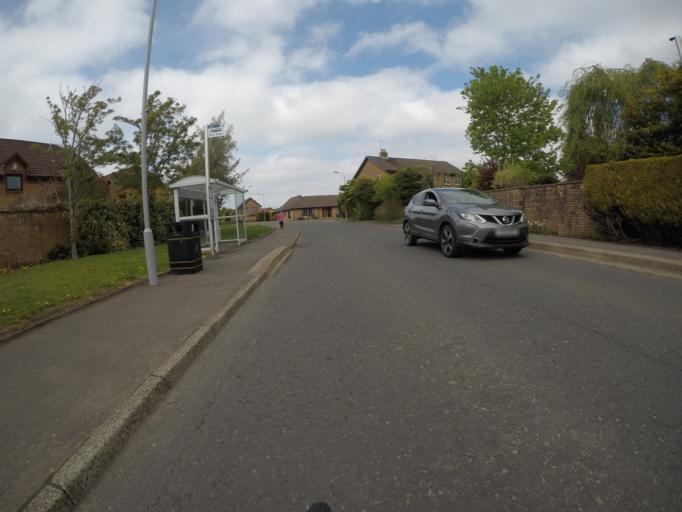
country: GB
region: Scotland
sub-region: East Renfrewshire
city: Newton Mearns
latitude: 55.7775
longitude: -4.3483
